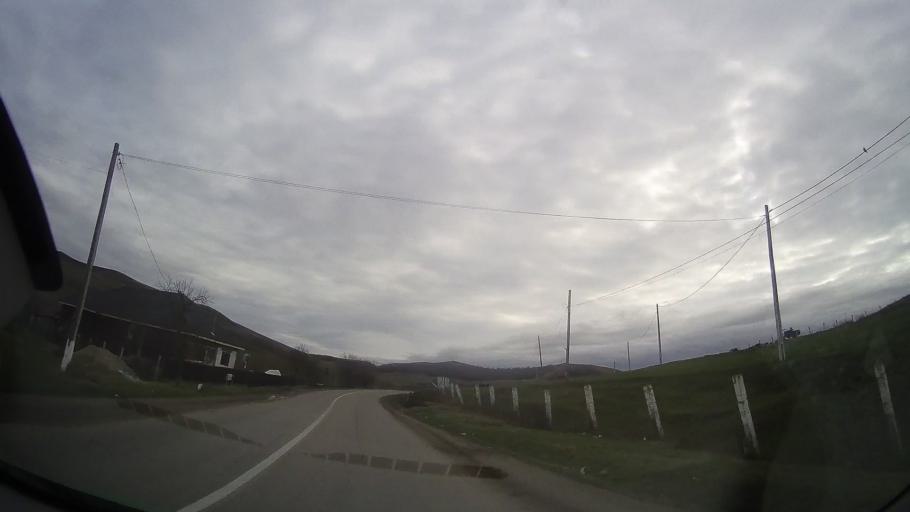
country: RO
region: Bistrita-Nasaud
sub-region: Comuna Budesti
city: Budesti
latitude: 46.8699
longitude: 24.2446
